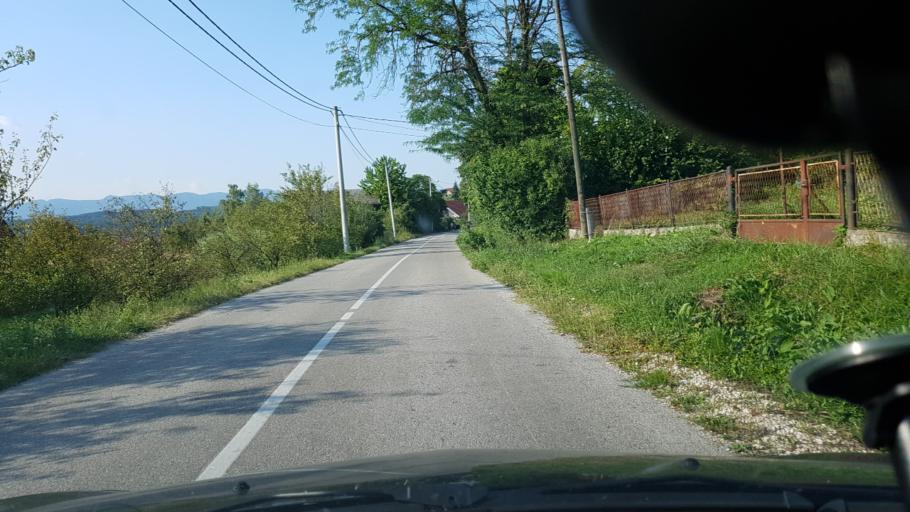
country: HR
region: Zagrebacka
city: Bregana
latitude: 45.8996
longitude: 15.6842
